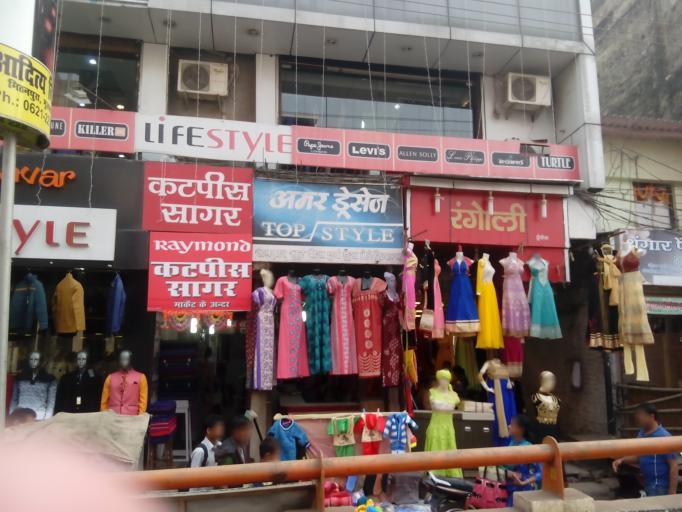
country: IN
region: Bihar
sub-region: Muzaffarpur
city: Muzaffarpur
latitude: 26.1193
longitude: 85.3883
